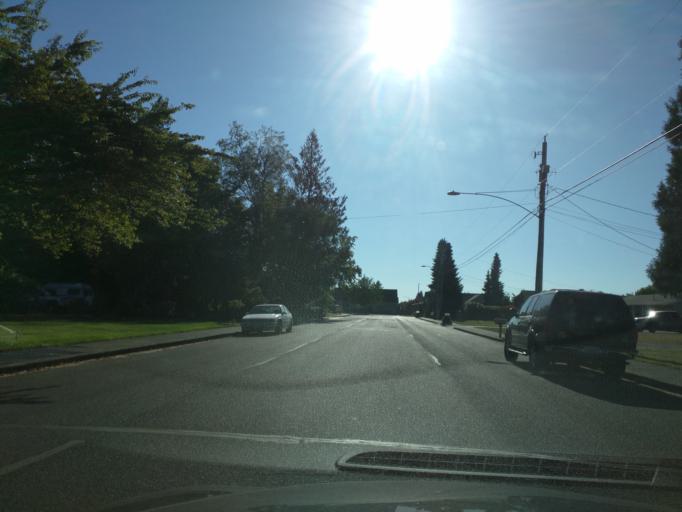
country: US
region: Washington
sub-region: Whatcom County
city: Lynden
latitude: 48.9508
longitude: -122.4560
